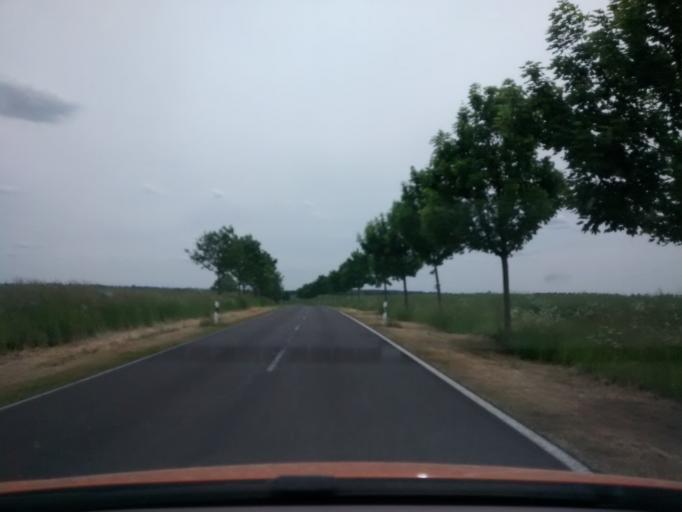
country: DE
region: Brandenburg
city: Juterbog
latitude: 51.9682
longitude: 13.0757
